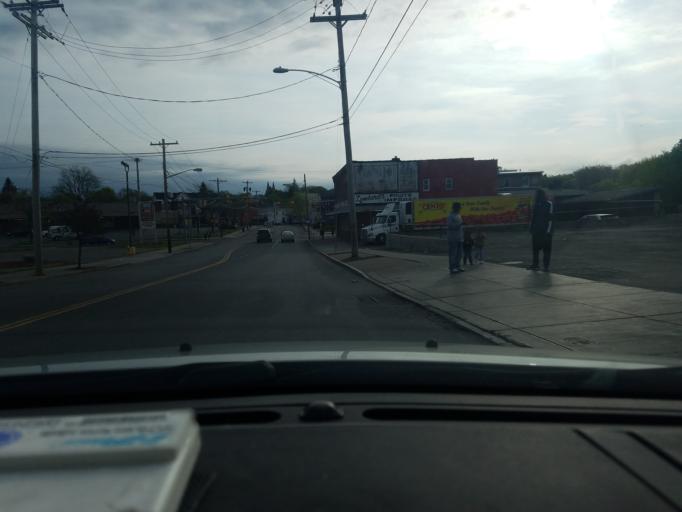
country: US
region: New York
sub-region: Onondaga County
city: Syracuse
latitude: 43.0594
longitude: -76.1482
